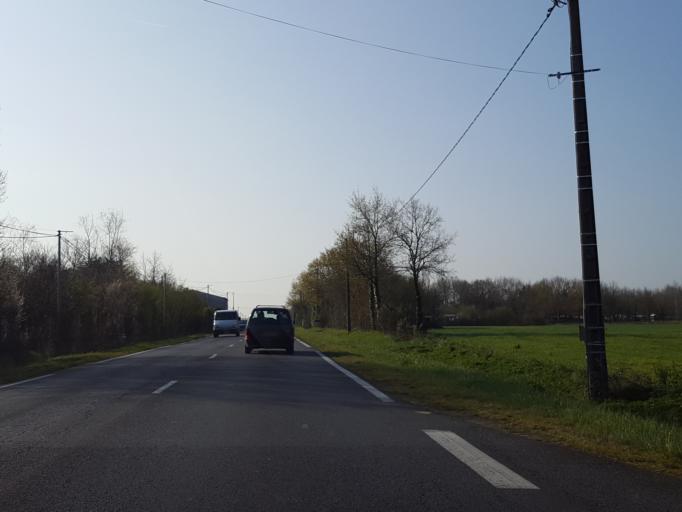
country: FR
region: Pays de la Loire
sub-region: Departement de la Loire-Atlantique
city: Le Bignon
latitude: 47.0969
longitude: -1.5326
